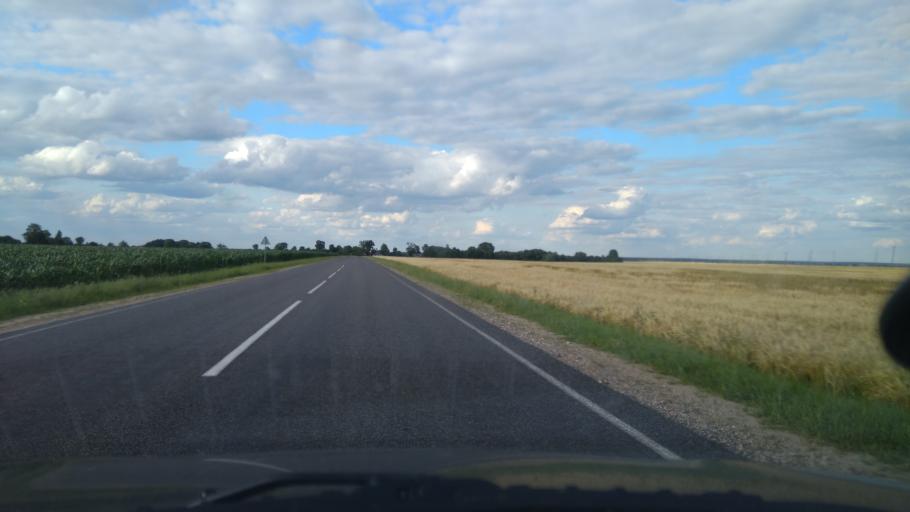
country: BY
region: Grodnenskaya
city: Masty
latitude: 53.3065
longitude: 24.6921
